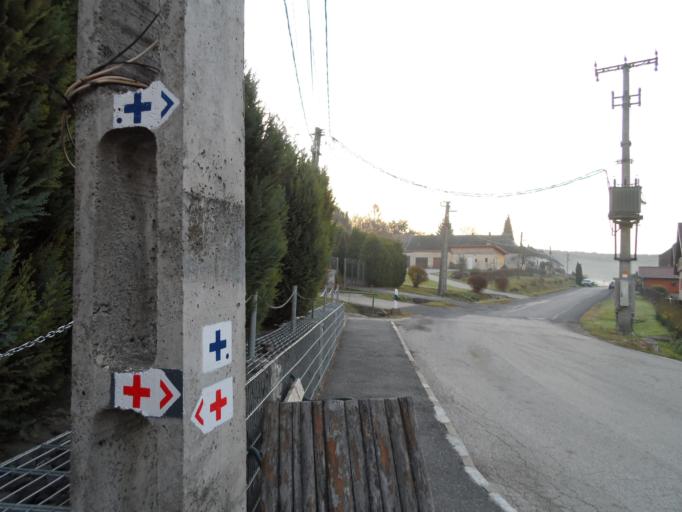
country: HU
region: Veszprem
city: Herend
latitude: 47.1815
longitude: 17.6840
